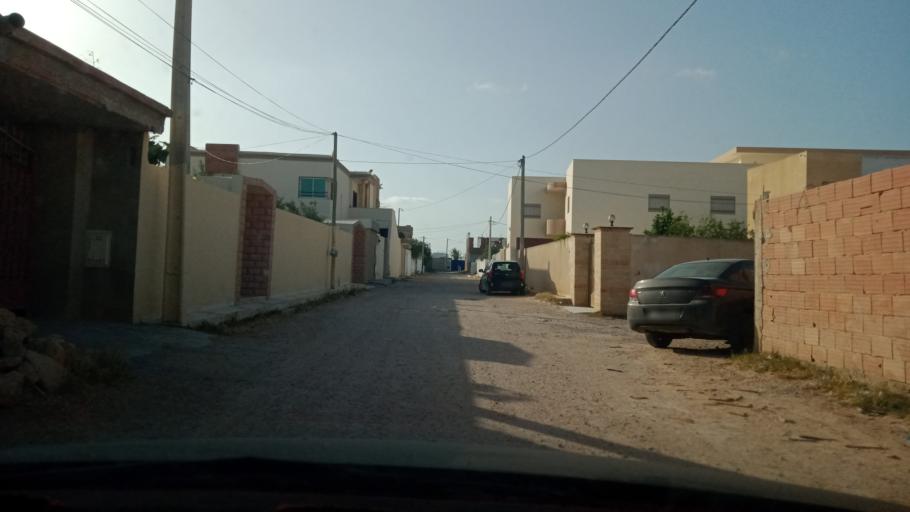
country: TN
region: Safaqis
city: Sfax
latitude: 34.8152
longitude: 10.7380
